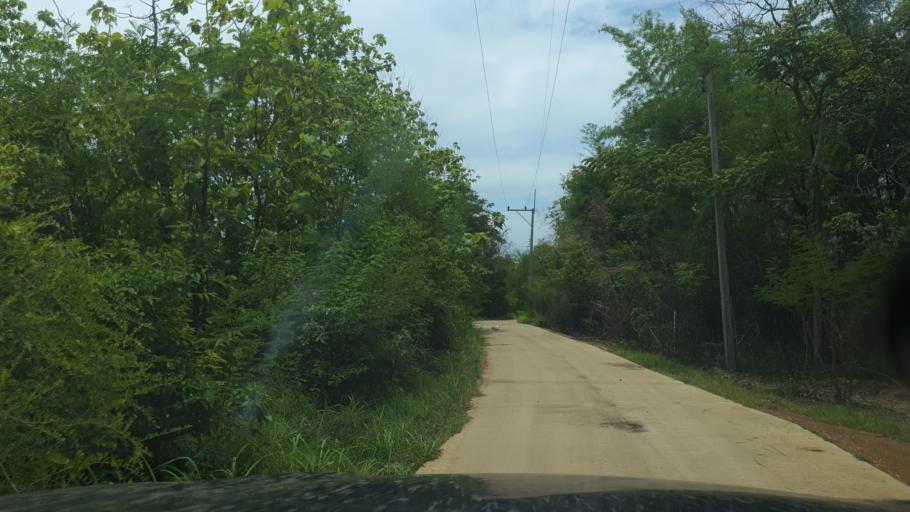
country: TH
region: Lampang
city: Ko Kha
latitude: 18.1330
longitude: 99.3332
